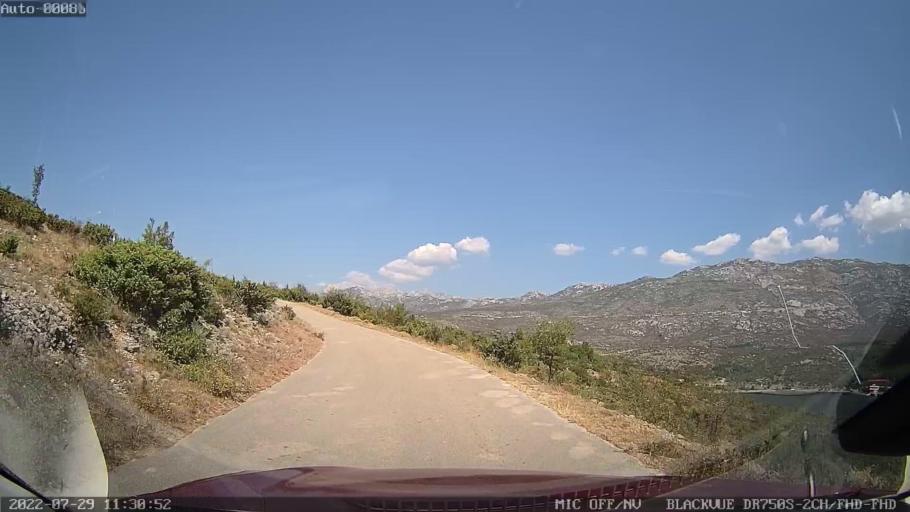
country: HR
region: Zadarska
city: Obrovac
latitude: 44.1987
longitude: 15.7491
